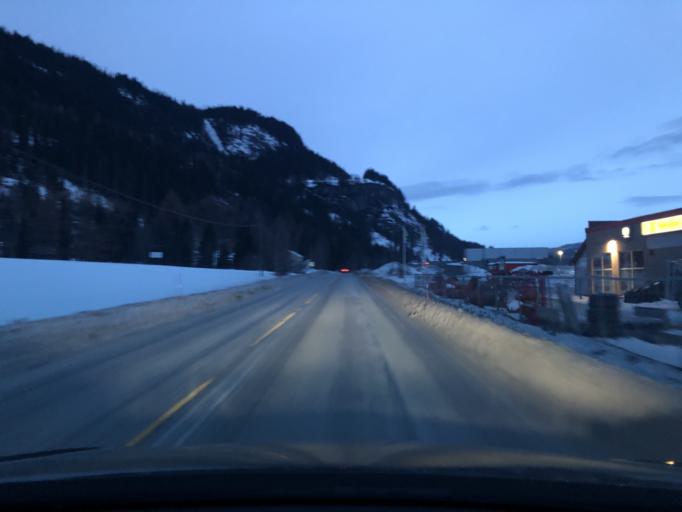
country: NO
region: Oppland
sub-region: Nord-Aurdal
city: Fagernes
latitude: 60.9949
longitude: 9.2158
